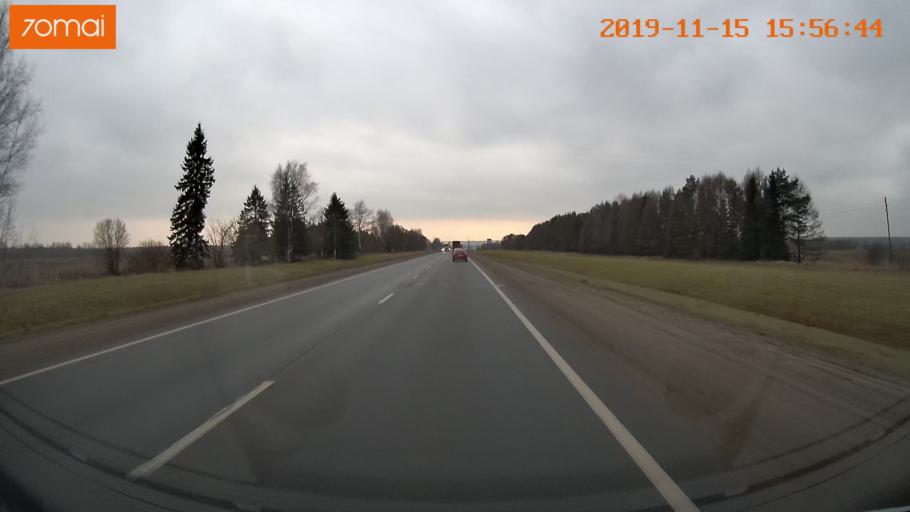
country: RU
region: Jaroslavl
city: Yaroslavl
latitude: 57.8386
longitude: 39.9703
